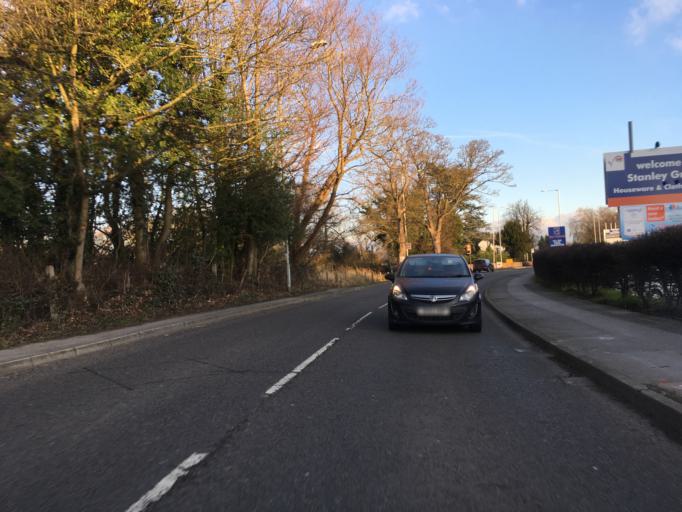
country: GB
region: England
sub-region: Borough of Stockport
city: Cheadle Hulme
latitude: 53.3593
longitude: -2.2035
